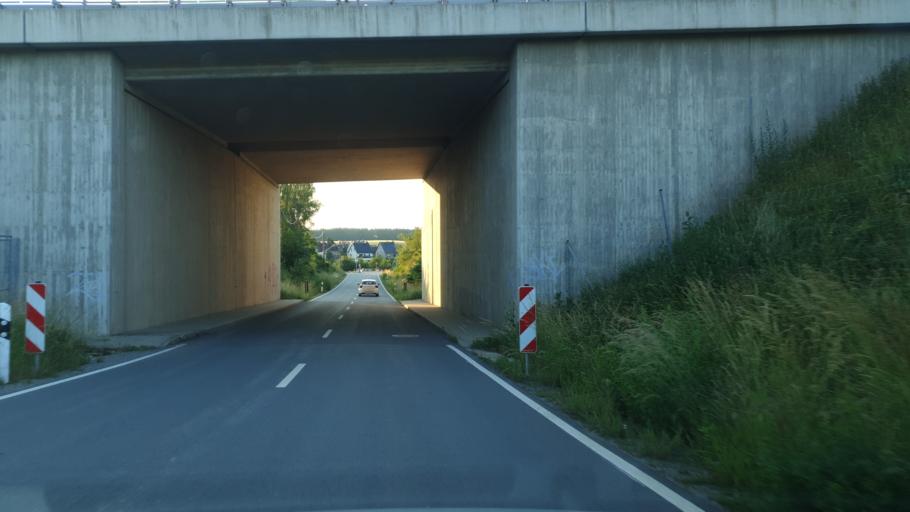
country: DE
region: Saxony
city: Oelsnitz
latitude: 50.6943
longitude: 12.7284
